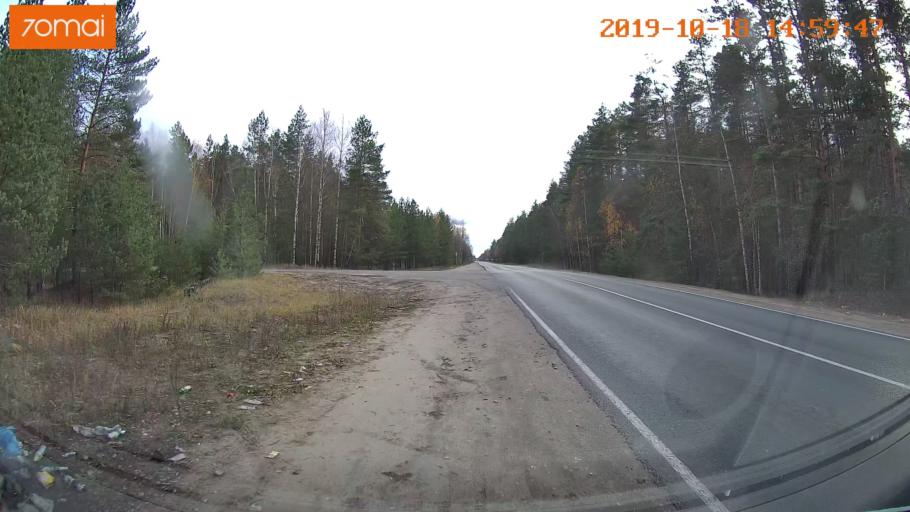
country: RU
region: Vladimir
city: Kurlovo
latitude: 55.4978
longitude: 40.5743
